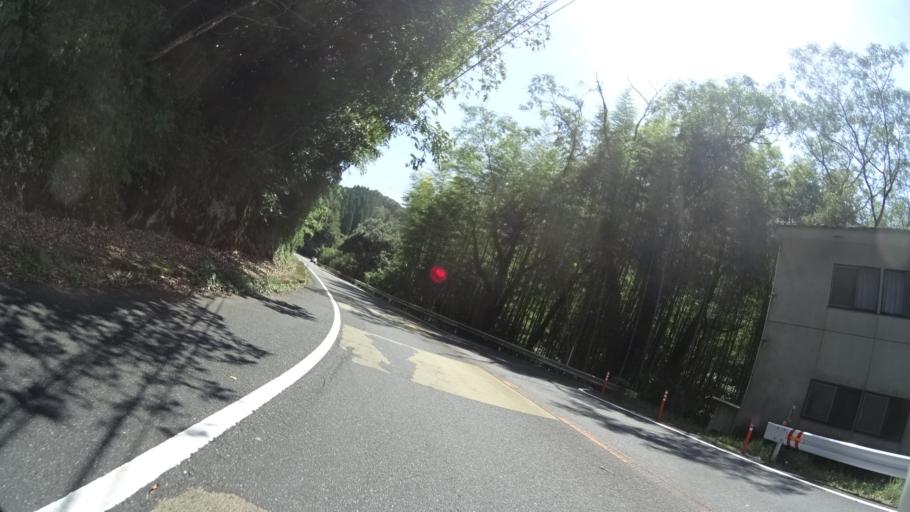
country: JP
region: Kagoshima
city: Kokubu-matsuki
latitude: 31.8405
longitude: 130.7486
